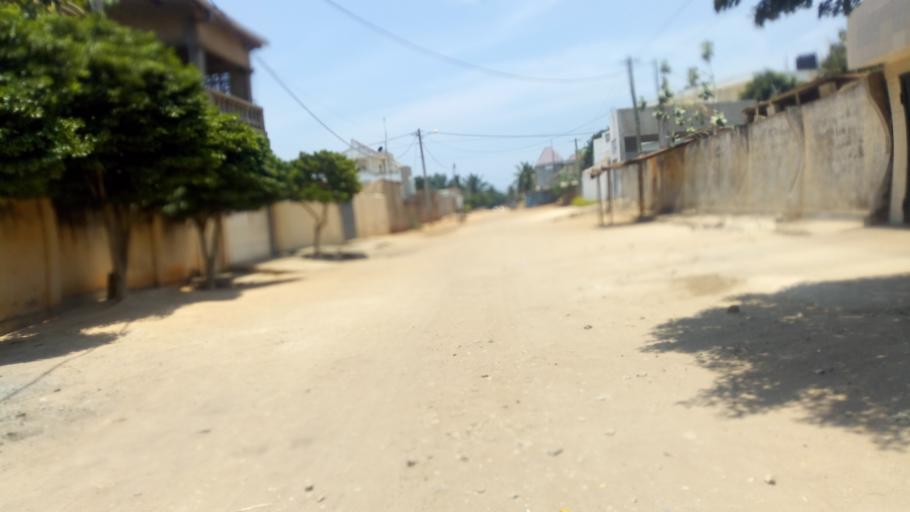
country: TG
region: Maritime
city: Lome
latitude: 6.1911
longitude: 1.1786
